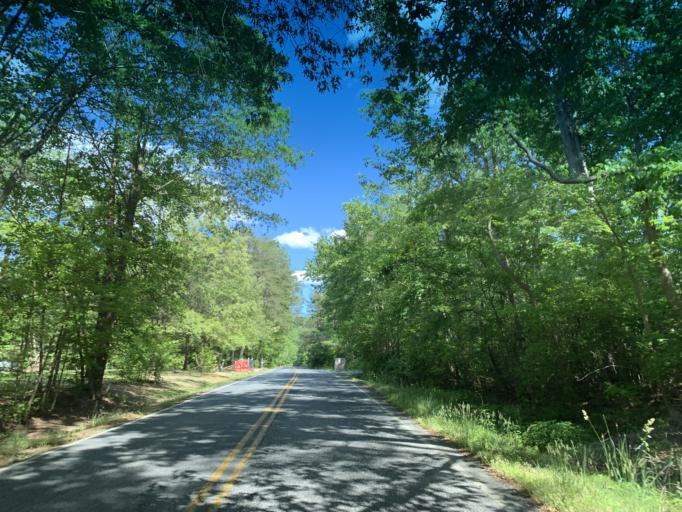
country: US
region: Maryland
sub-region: Cecil County
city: Charlestown
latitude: 39.5416
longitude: -75.9252
